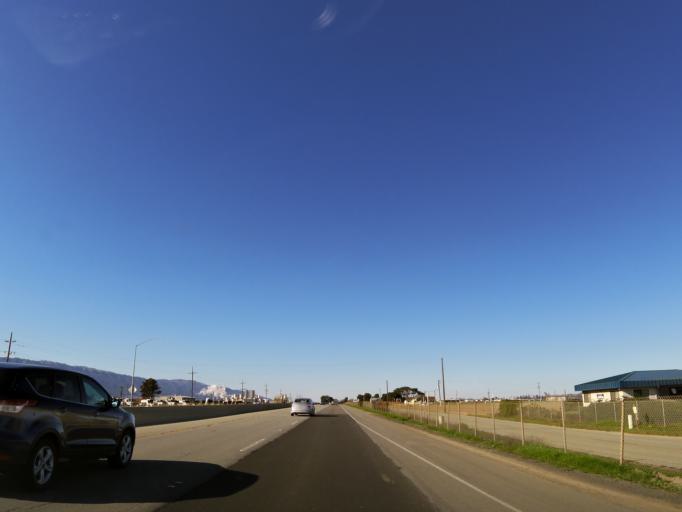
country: US
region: California
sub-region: Monterey County
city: Soledad
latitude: 36.4513
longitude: -121.3660
